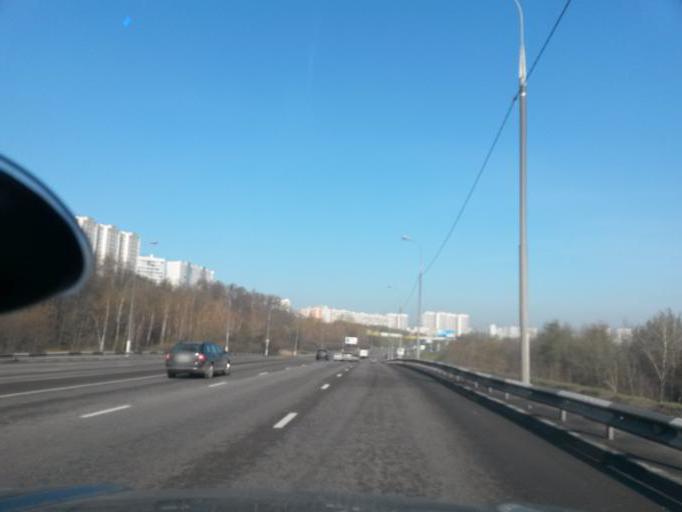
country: RU
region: Moscow
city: Zyablikovo
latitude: 55.6209
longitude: 37.7661
